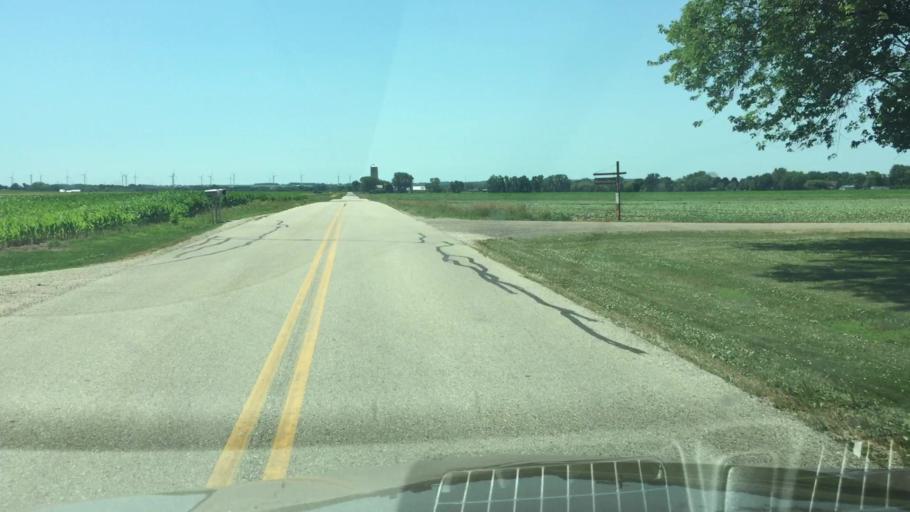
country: US
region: Wisconsin
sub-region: Fond du Lac County
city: Saint Peter
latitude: 43.9606
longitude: -88.3116
